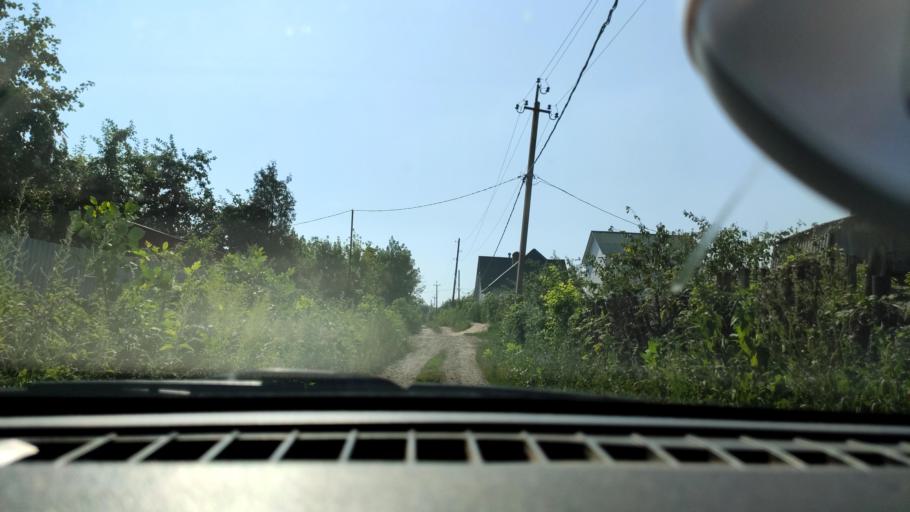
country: RU
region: Samara
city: Petra-Dubrava
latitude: 53.2691
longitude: 50.2956
